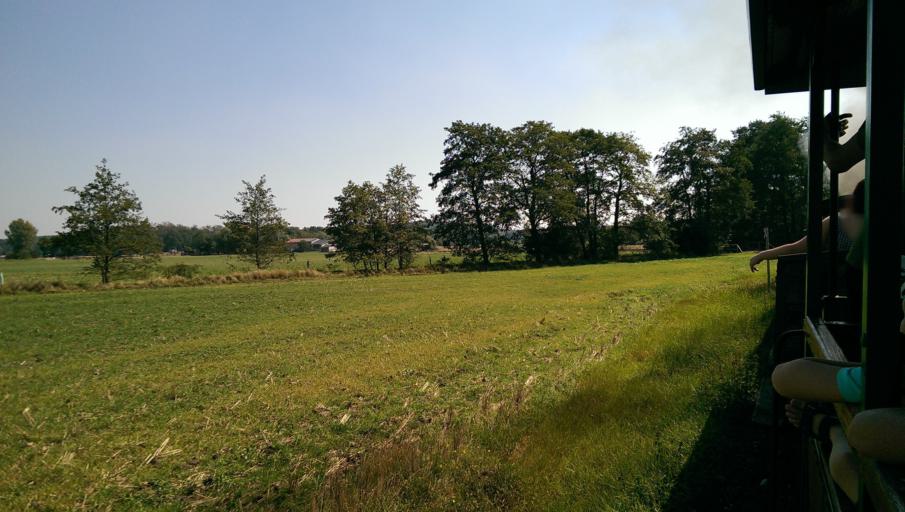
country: CZ
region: Central Bohemia
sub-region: Okres Kolin
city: Kolin
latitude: 50.0534
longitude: 15.2517
